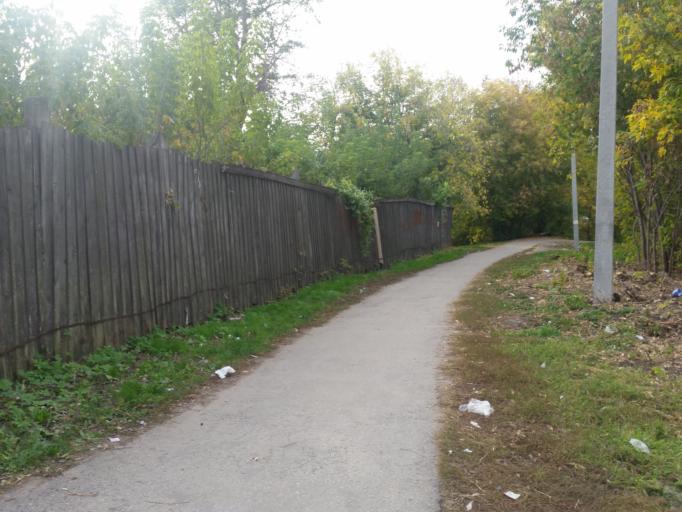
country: RU
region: Ulyanovsk
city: Dimitrovgrad
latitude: 54.2163
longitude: 49.6204
